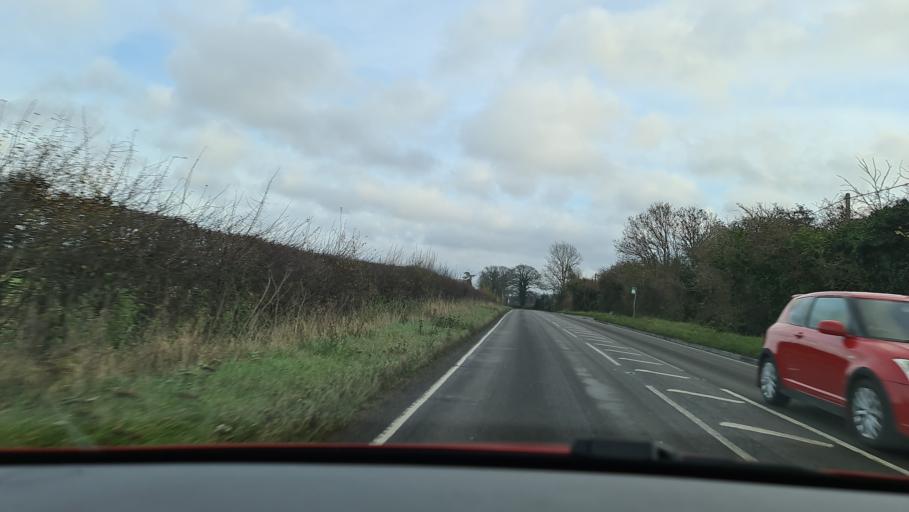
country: GB
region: England
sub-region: Buckinghamshire
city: Weston Turville
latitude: 51.7616
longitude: -0.7936
